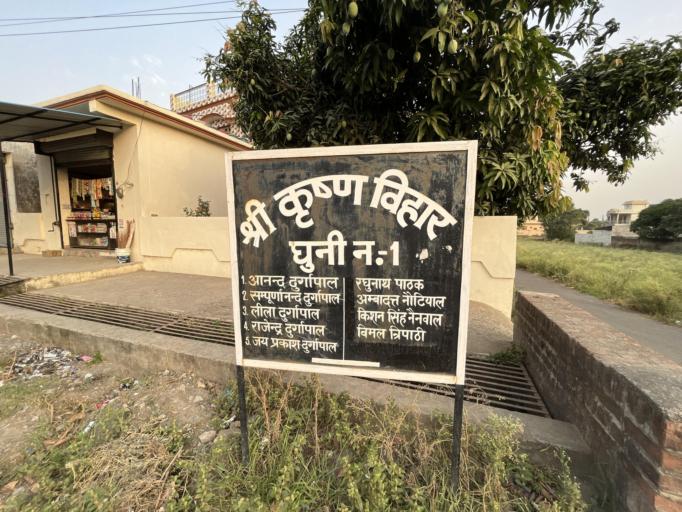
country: IN
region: Uttarakhand
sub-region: Naini Tal
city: Haldwani
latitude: 29.2291
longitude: 79.4746
